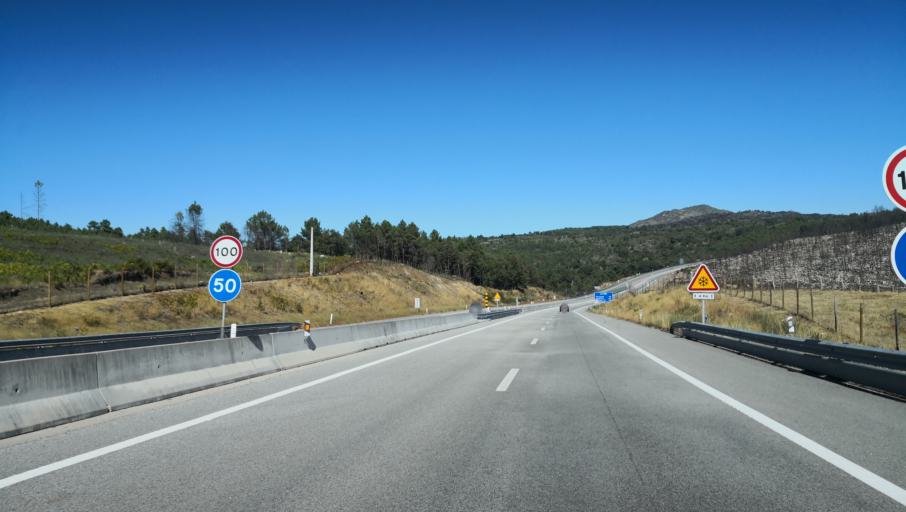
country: PT
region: Vila Real
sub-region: Sabrosa
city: Sabrosa
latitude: 41.3532
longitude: -7.5982
